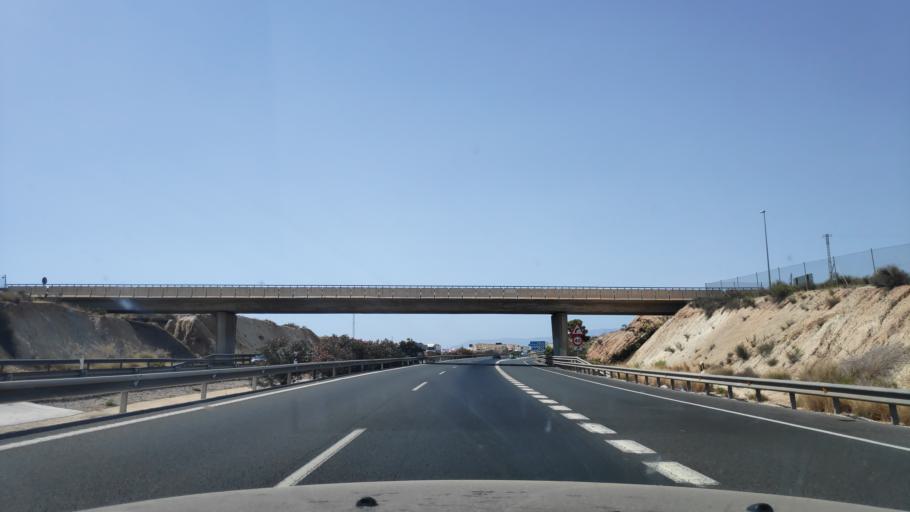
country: ES
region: Murcia
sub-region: Murcia
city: Molina de Segura
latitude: 38.0603
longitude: -1.1900
